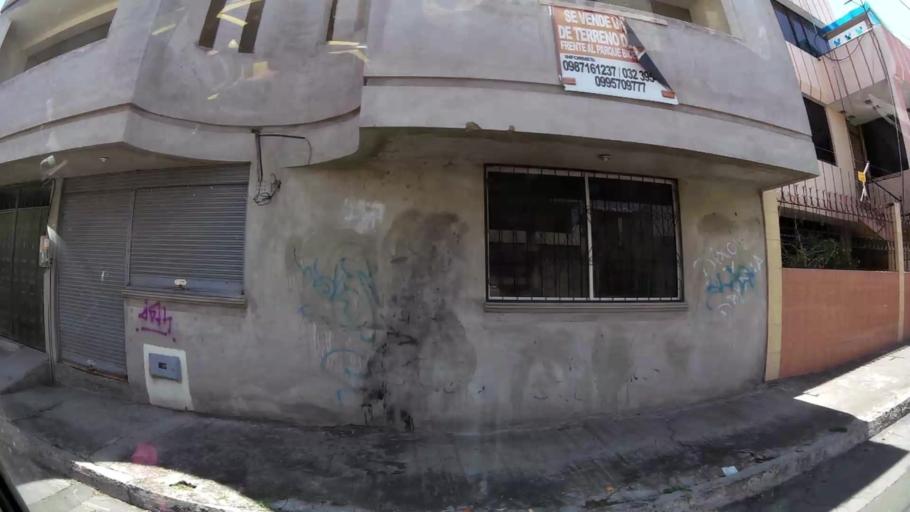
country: EC
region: Chimborazo
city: Riobamba
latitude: -1.6731
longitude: -78.6608
